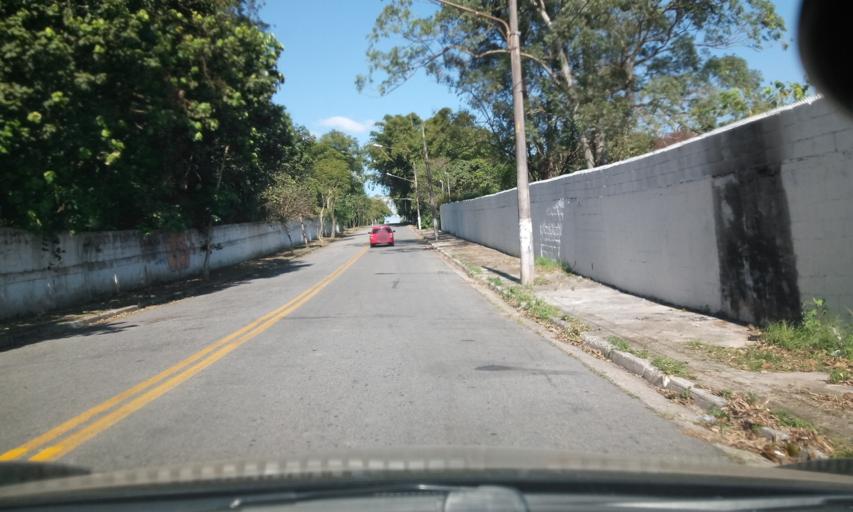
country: BR
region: Sao Paulo
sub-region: Sao Bernardo Do Campo
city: Sao Bernardo do Campo
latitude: -23.7147
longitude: -46.5776
